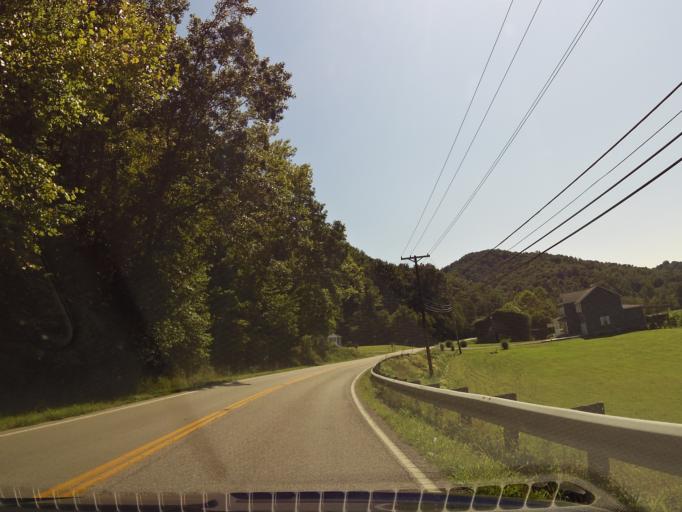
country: US
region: Kentucky
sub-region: Clay County
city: Manchester
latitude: 37.1089
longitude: -83.7149
